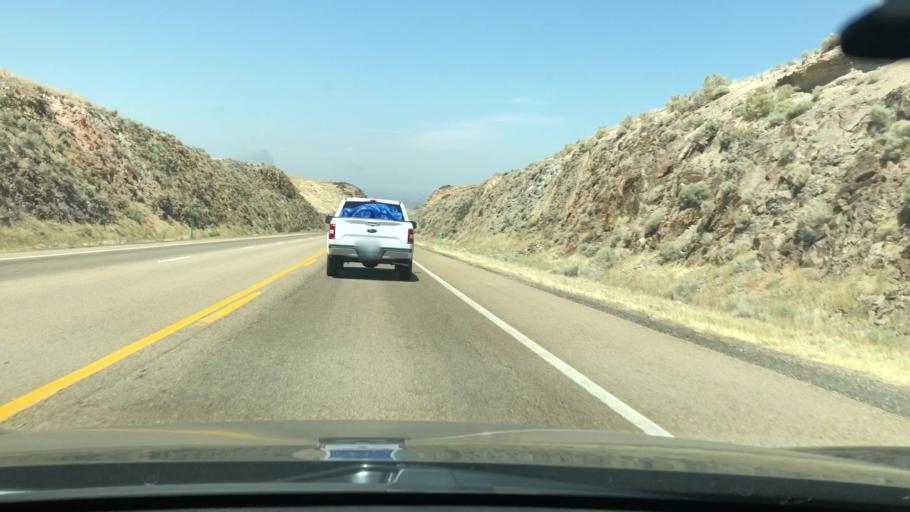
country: US
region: Idaho
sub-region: Owyhee County
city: Marsing
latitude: 43.4282
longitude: -116.8589
